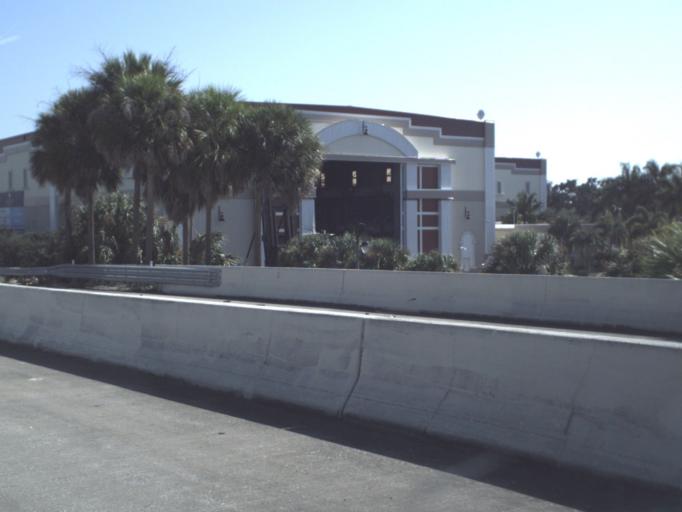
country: US
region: Florida
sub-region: Pinellas County
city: Gulfport
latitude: 27.7137
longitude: -82.6793
